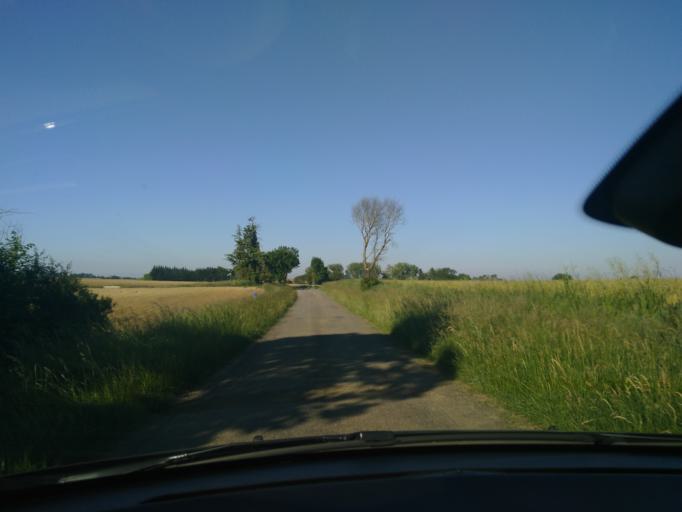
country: FR
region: Midi-Pyrenees
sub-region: Departement du Tarn-et-Garonne
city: Beaumont-de-Lomagne
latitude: 43.7803
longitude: 0.9588
